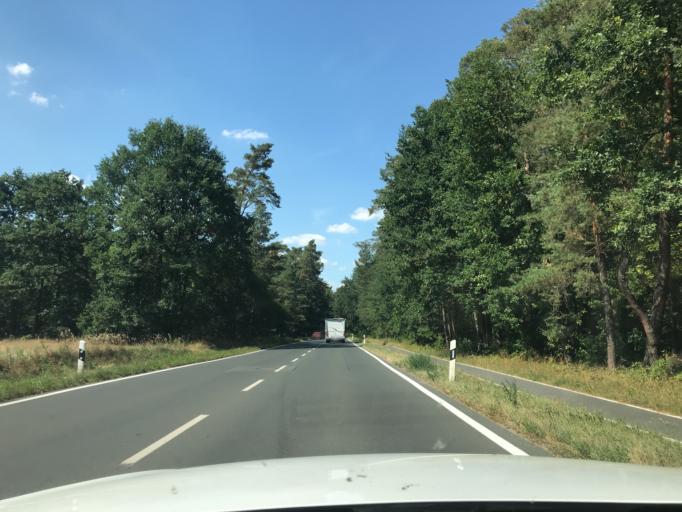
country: DE
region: Bavaria
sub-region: Regierungsbezirk Mittelfranken
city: Erlangen
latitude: 49.5571
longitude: 11.0155
